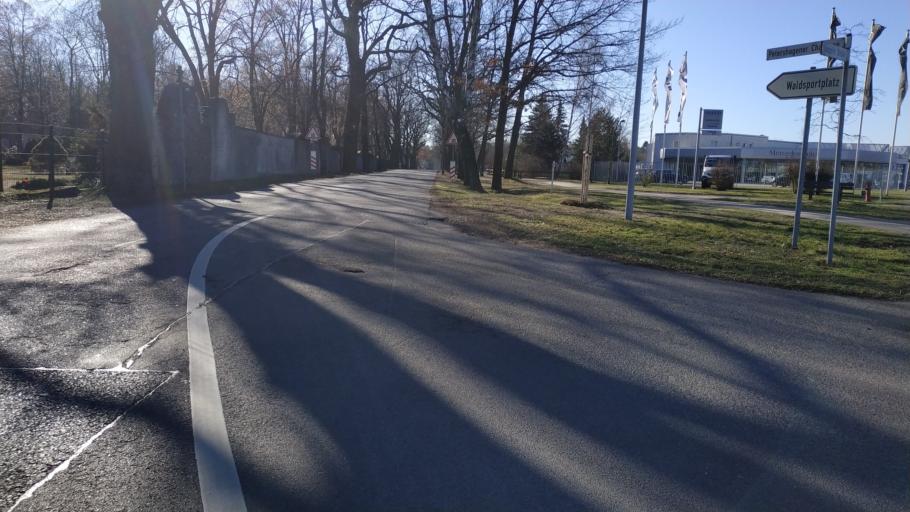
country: DE
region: Brandenburg
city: Petershagen
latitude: 52.5334
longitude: 13.8111
